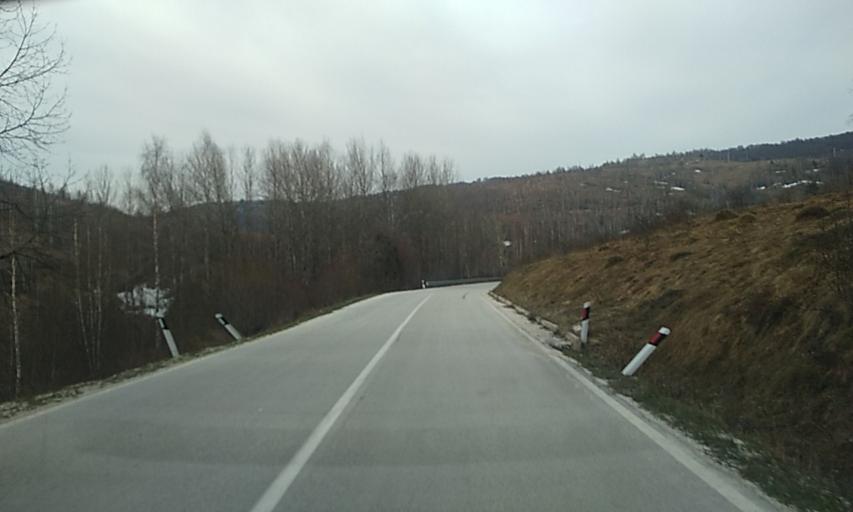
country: RS
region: Central Serbia
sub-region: Pcinjski Okrug
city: Bosilegrad
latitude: 42.6432
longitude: 22.3802
